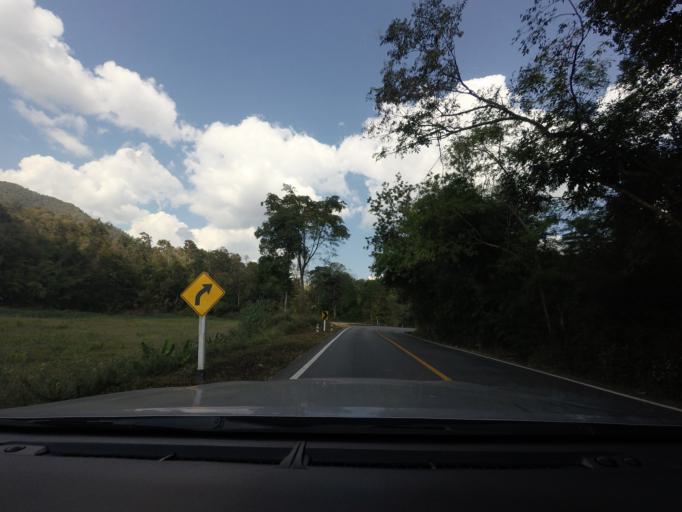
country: TH
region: Chiang Mai
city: Chai Prakan
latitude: 19.5697
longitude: 99.0817
